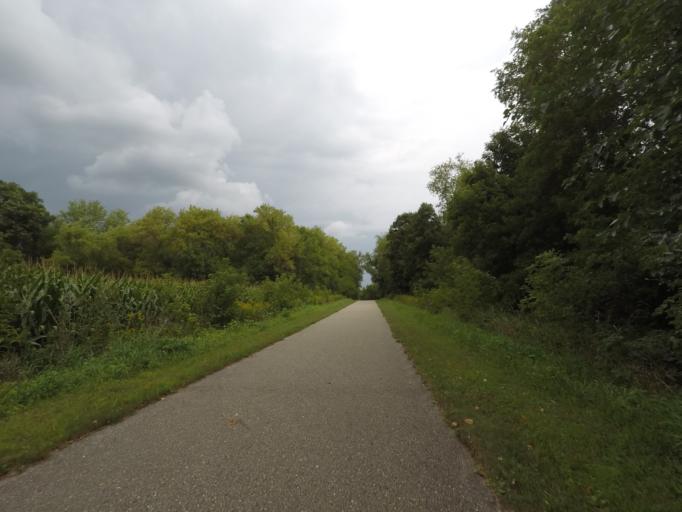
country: US
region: Wisconsin
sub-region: Jefferson County
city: Fort Atkinson
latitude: 42.9531
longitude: -88.8283
